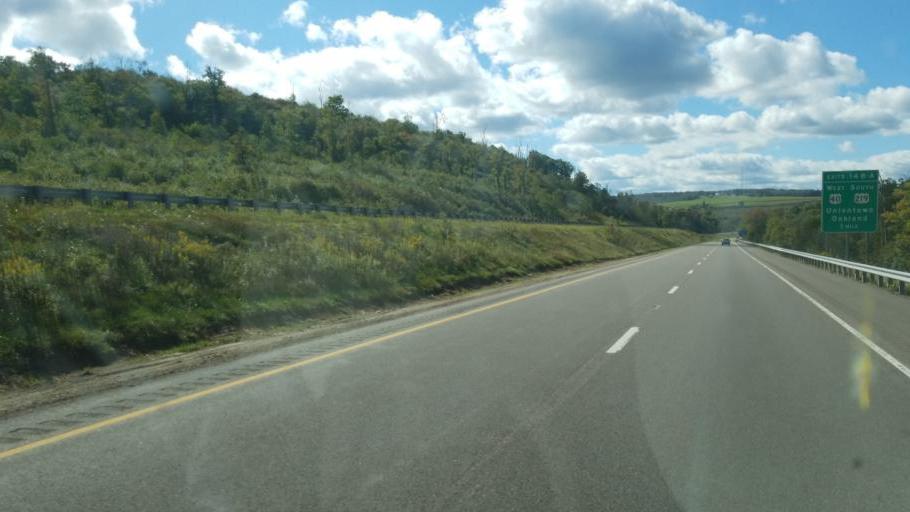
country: US
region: Pennsylvania
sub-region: Somerset County
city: Meyersdale
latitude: 39.6803
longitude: -79.2251
